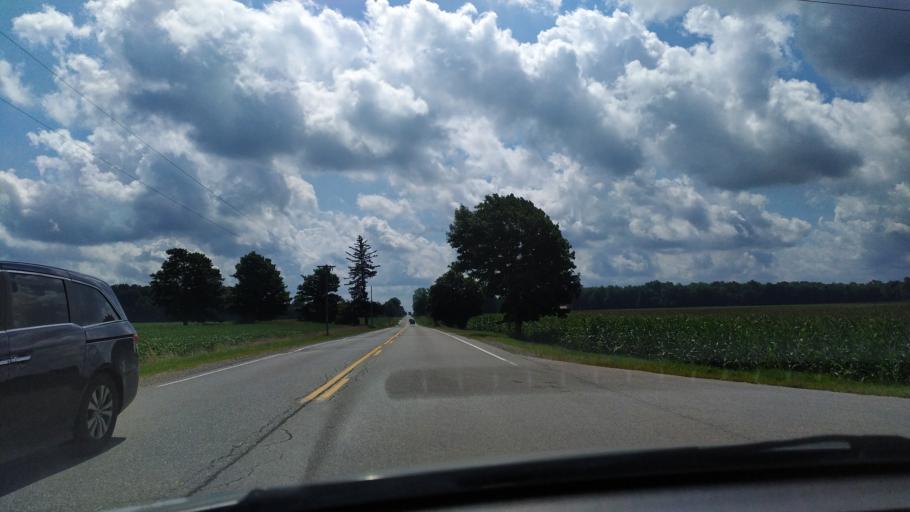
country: CA
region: Ontario
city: London
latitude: 43.0540
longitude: -81.3292
